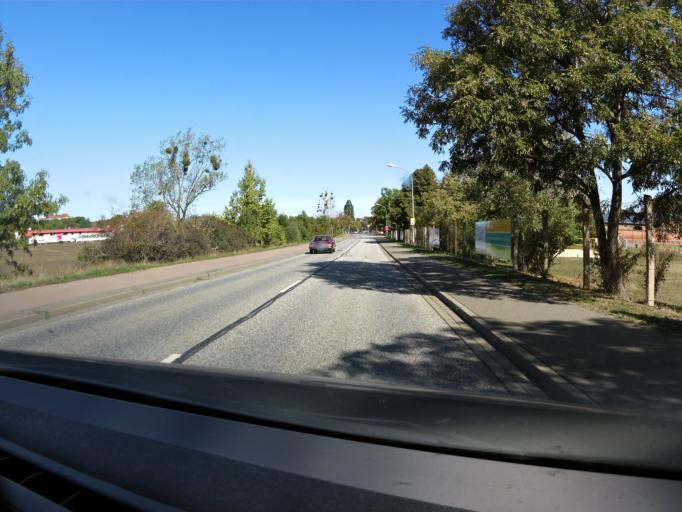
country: DE
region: Saxony-Anhalt
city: Quedlinburg
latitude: 51.7758
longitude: 11.1405
